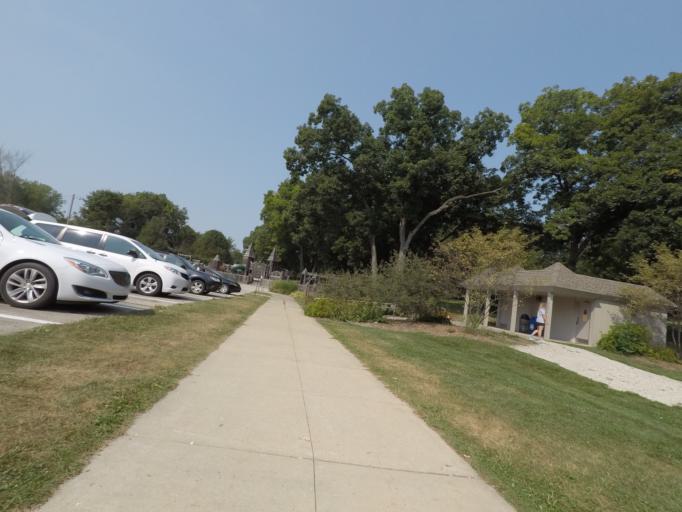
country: US
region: Wisconsin
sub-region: Waukesha County
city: Delafield
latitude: 43.0614
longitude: -88.4144
